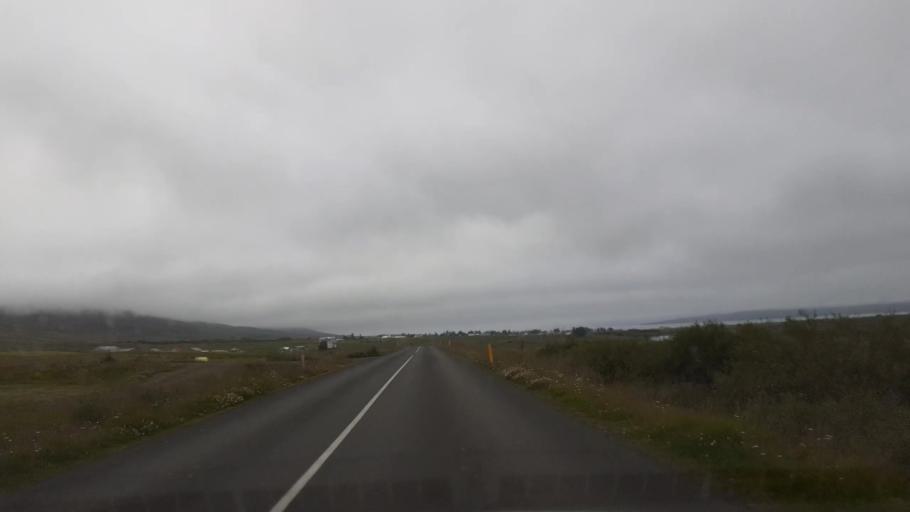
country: IS
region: Northeast
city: Dalvik
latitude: 65.9520
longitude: -18.5531
